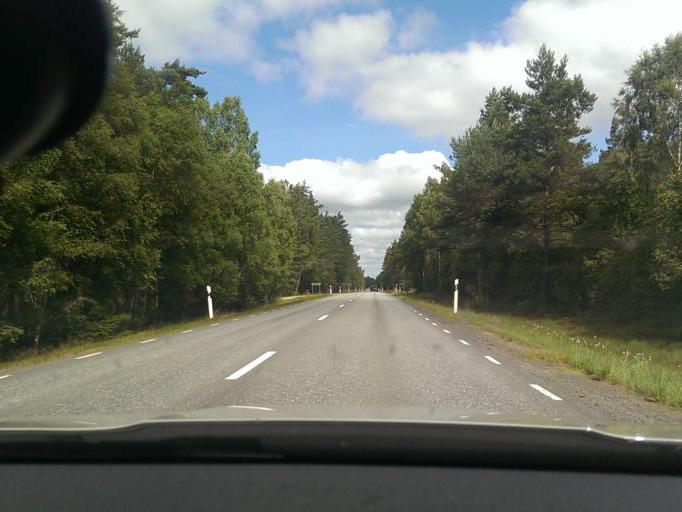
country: SE
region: Joenkoeping
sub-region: Gnosjo Kommun
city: Hillerstorp
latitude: 57.2983
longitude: 13.9297
